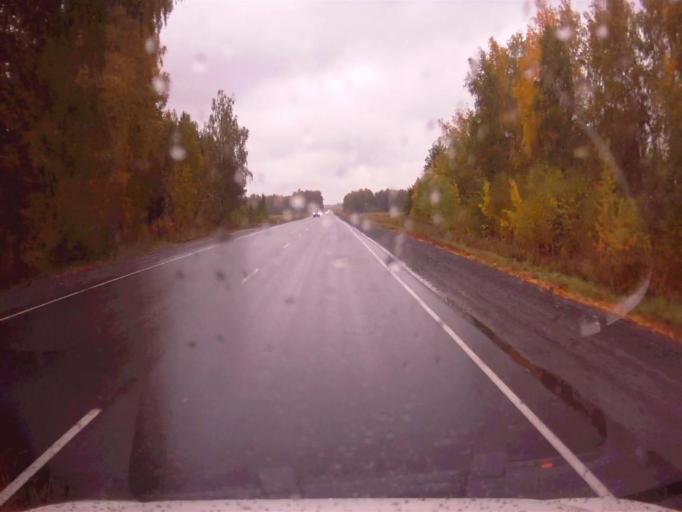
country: RU
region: Chelyabinsk
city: Roshchino
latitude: 55.3839
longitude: 61.1355
